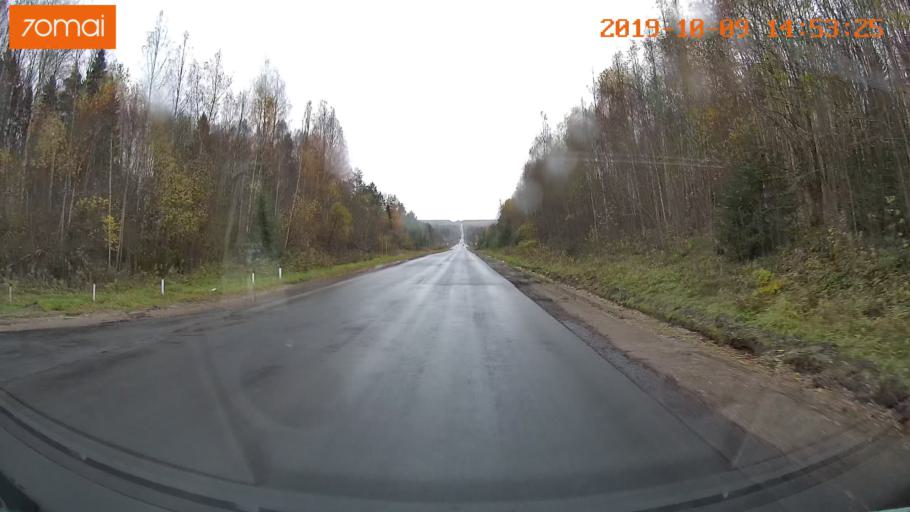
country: RU
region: Kostroma
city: Chistyye Bory
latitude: 58.3679
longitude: 41.6382
